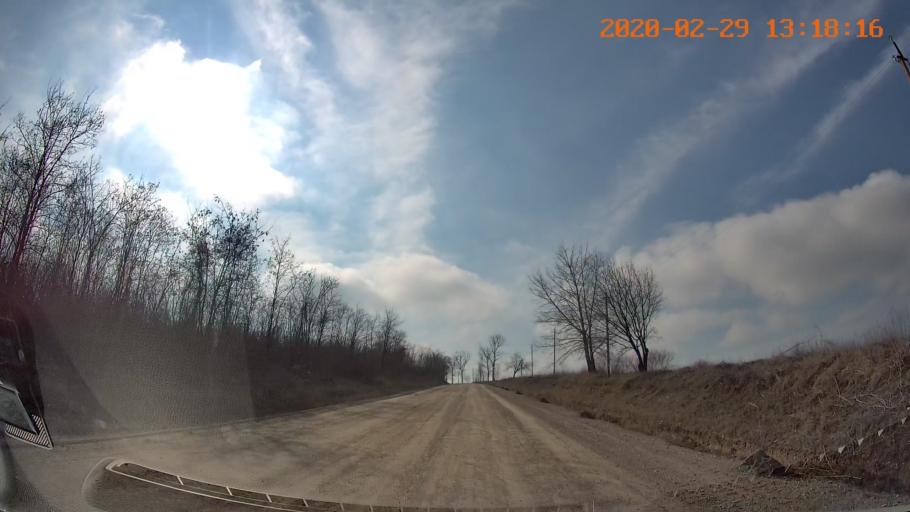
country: MD
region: Telenesti
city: Camenca
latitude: 47.9942
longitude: 28.6584
